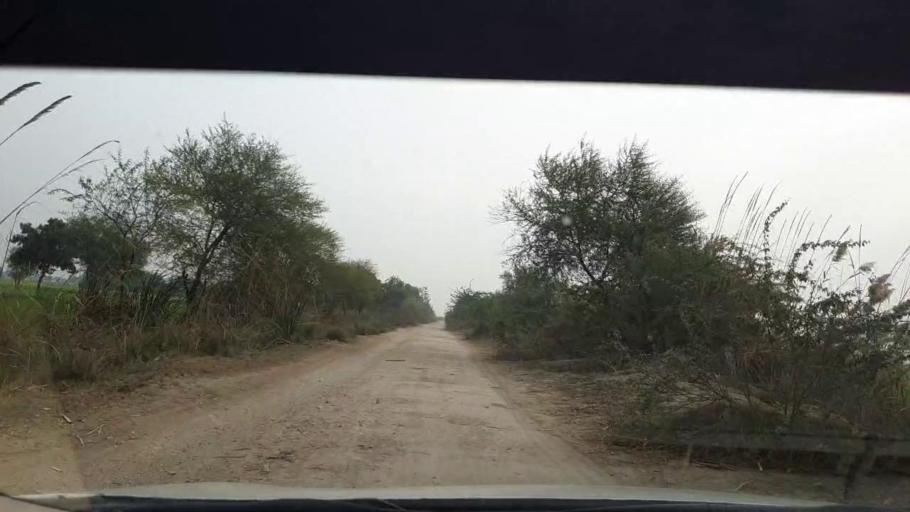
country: PK
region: Sindh
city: Berani
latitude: 25.8637
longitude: 68.8313
